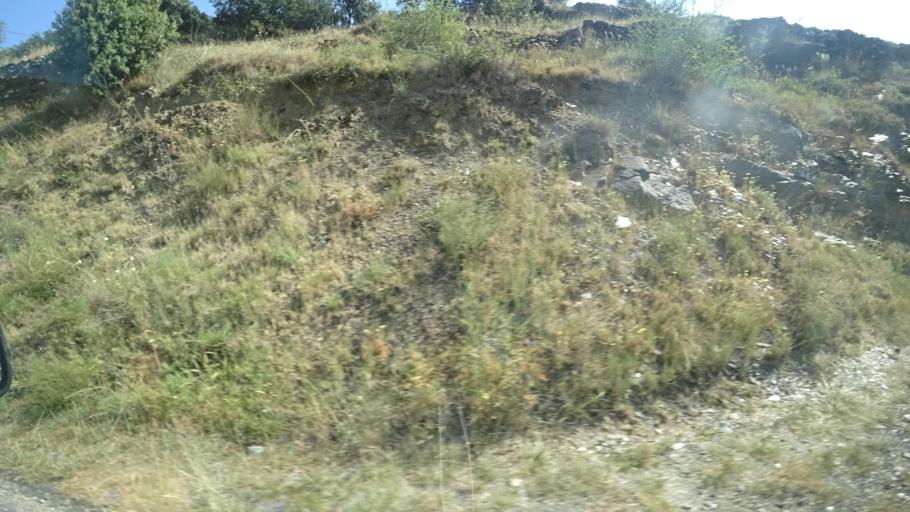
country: FR
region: Languedoc-Roussillon
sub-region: Departement des Pyrenees-Orientales
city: Vernet-les-Bains
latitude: 42.5677
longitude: 2.2953
